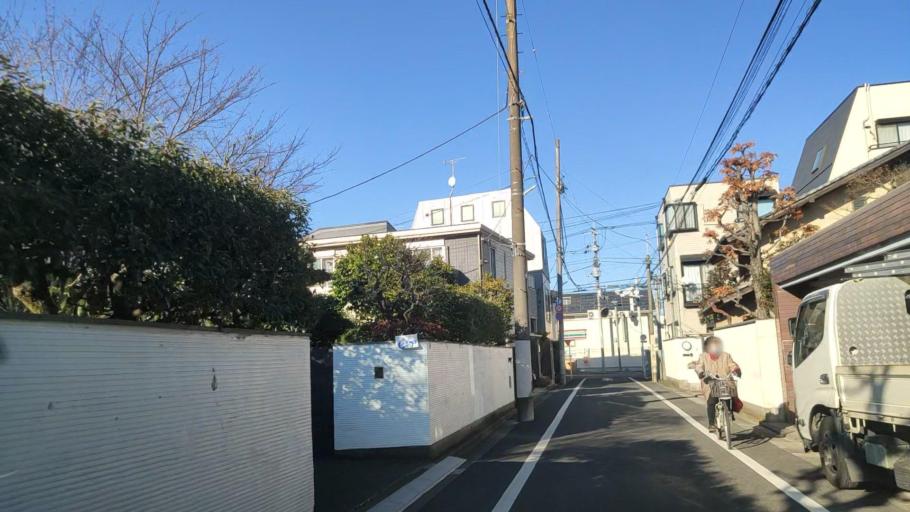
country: JP
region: Tokyo
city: Musashino
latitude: 35.6969
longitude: 139.5989
